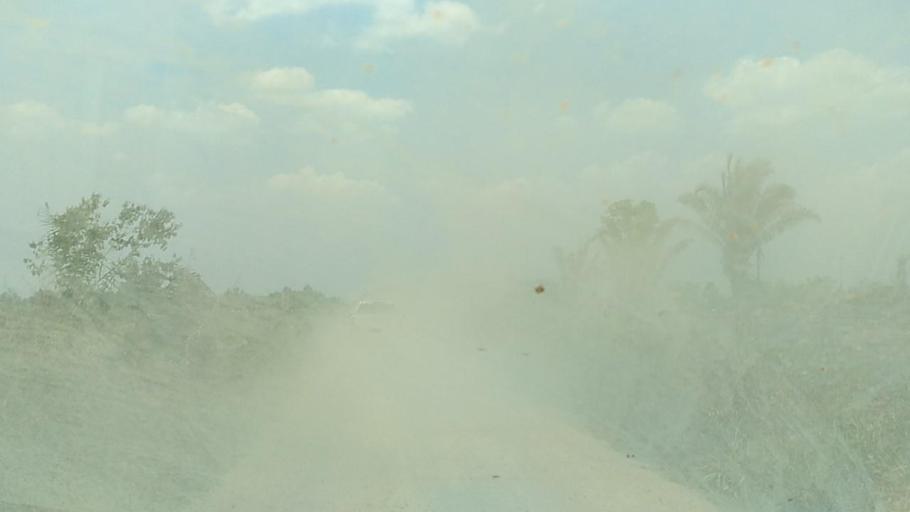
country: BR
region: Rondonia
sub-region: Porto Velho
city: Porto Velho
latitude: -8.7289
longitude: -63.2914
